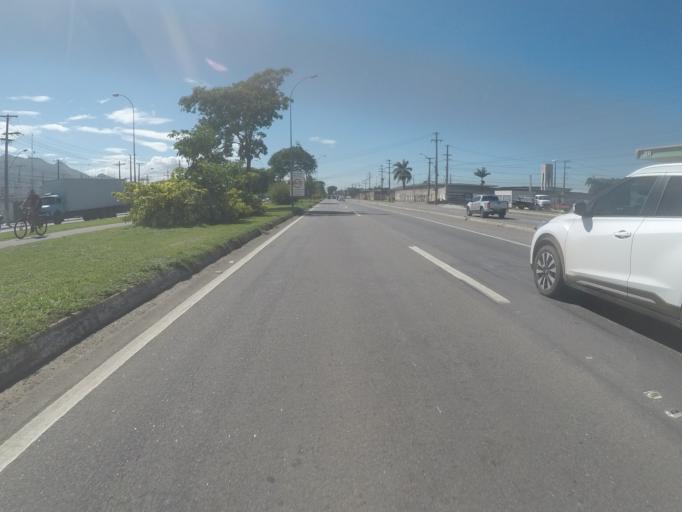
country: BR
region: Espirito Santo
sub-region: Serra
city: Serra
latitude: -20.2144
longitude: -40.2698
